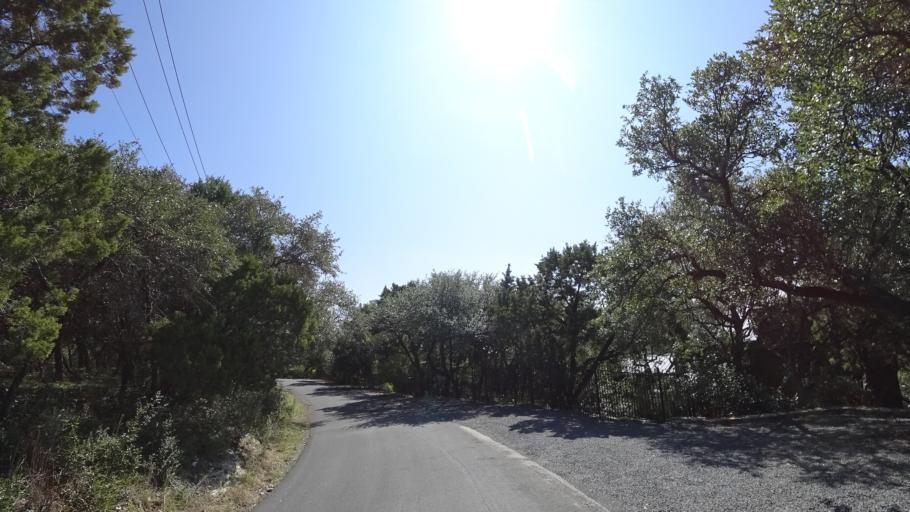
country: US
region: Texas
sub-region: Travis County
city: West Lake Hills
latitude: 30.3022
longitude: -97.7903
